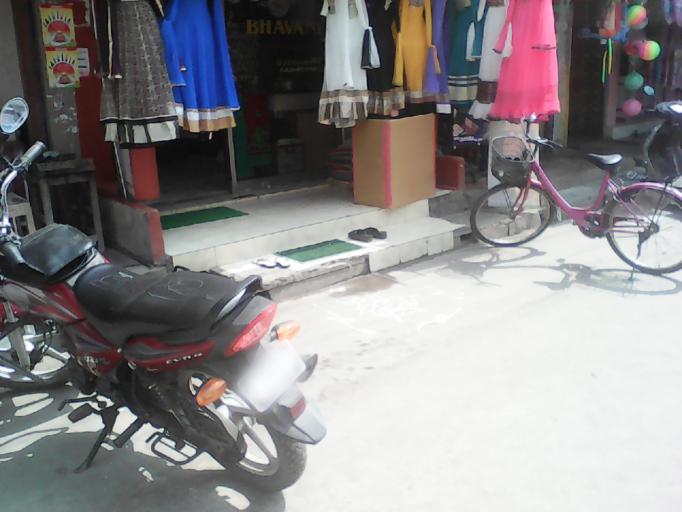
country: IN
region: Andhra Pradesh
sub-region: Guntur
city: Mangalagiri
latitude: 16.2391
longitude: 80.6496
